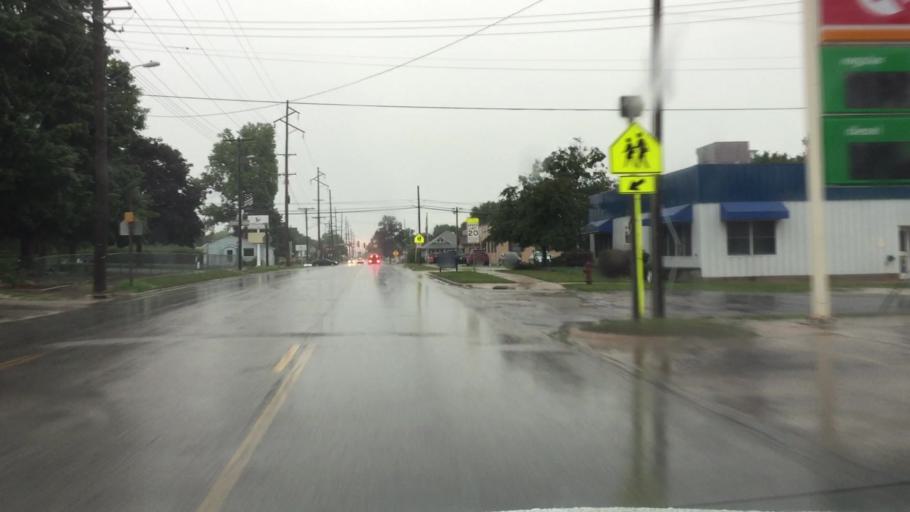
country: US
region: Illinois
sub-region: Hancock County
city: Carthage
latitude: 40.4163
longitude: -91.1325
